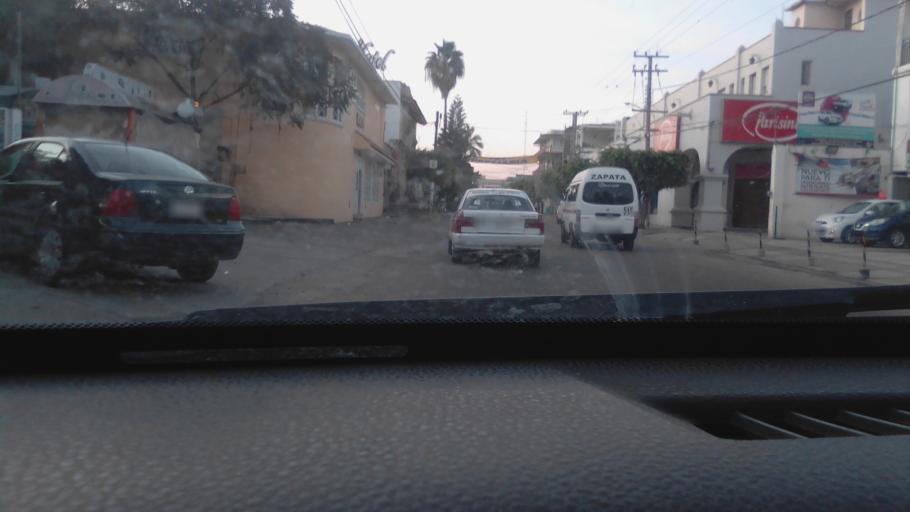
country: MX
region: Guerrero
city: Chilpancingo de los Bravos
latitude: 17.5587
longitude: -99.5060
